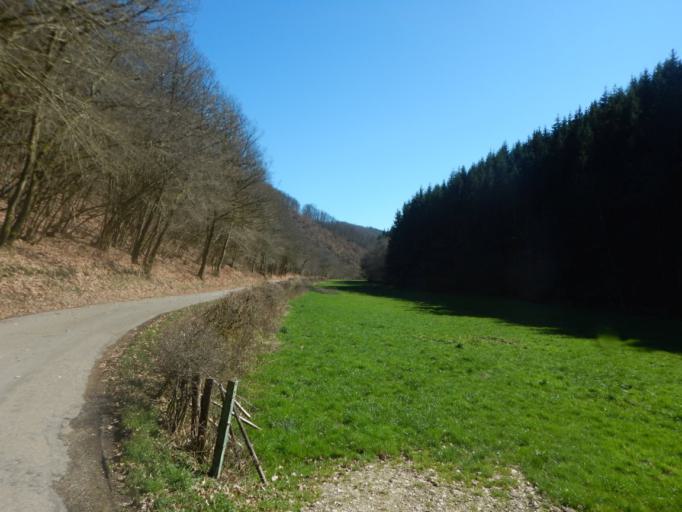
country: LU
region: Diekirch
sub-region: Canton de Wiltz
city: Eschweiler
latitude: 49.9717
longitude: 5.9605
